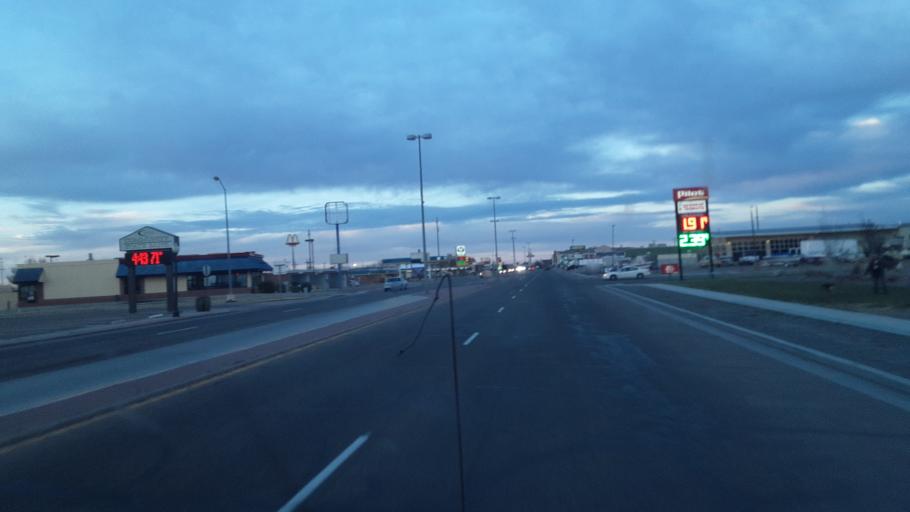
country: US
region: Colorado
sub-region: Prowers County
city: Lamar
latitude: 38.0967
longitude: -102.6196
